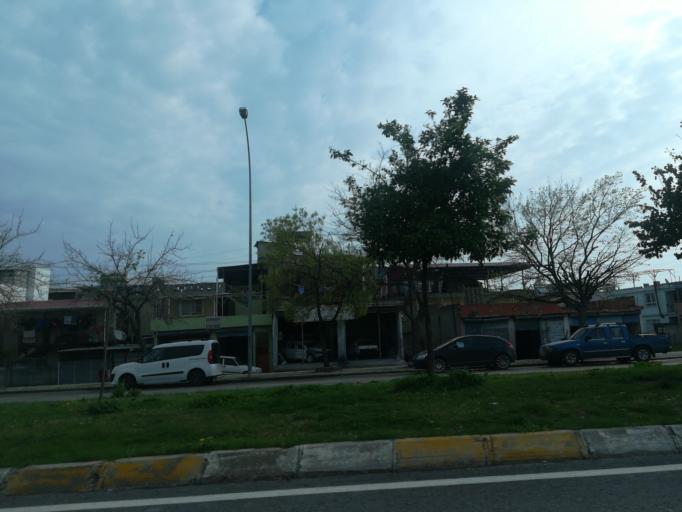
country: TR
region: Adana
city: Yuregir
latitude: 36.9956
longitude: 35.3593
